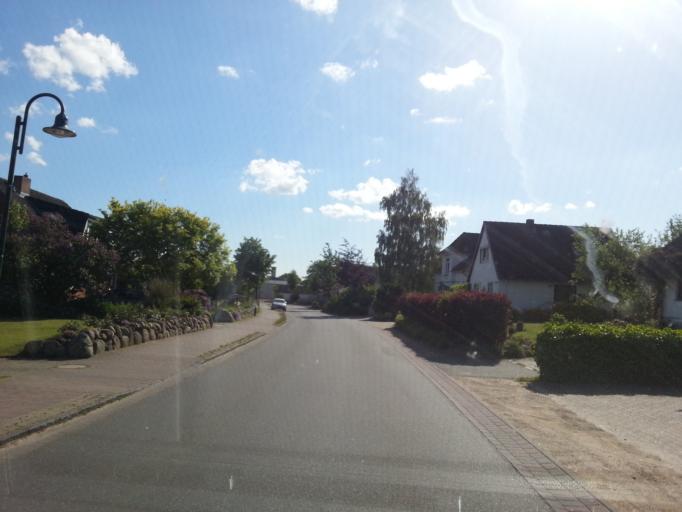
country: DE
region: Schleswig-Holstein
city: Scharbeutz
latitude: 54.0044
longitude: 10.7246
